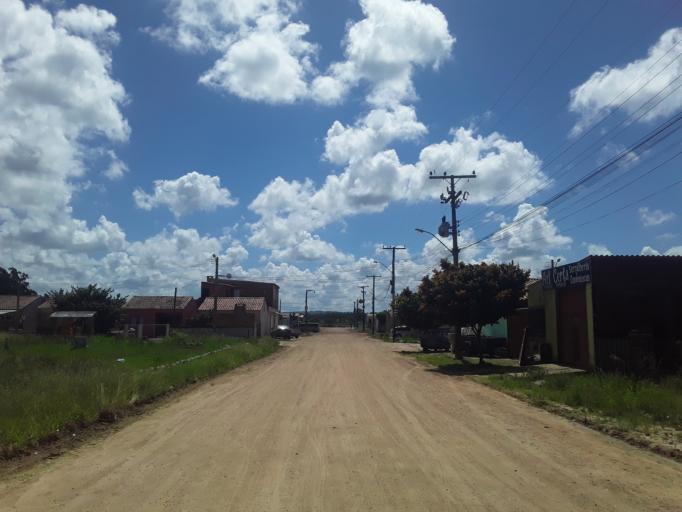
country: BR
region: Rio Grande do Sul
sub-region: Sao Lourenco Do Sul
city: Sao Lourenco do Sul
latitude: -31.3385
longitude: -51.9901
